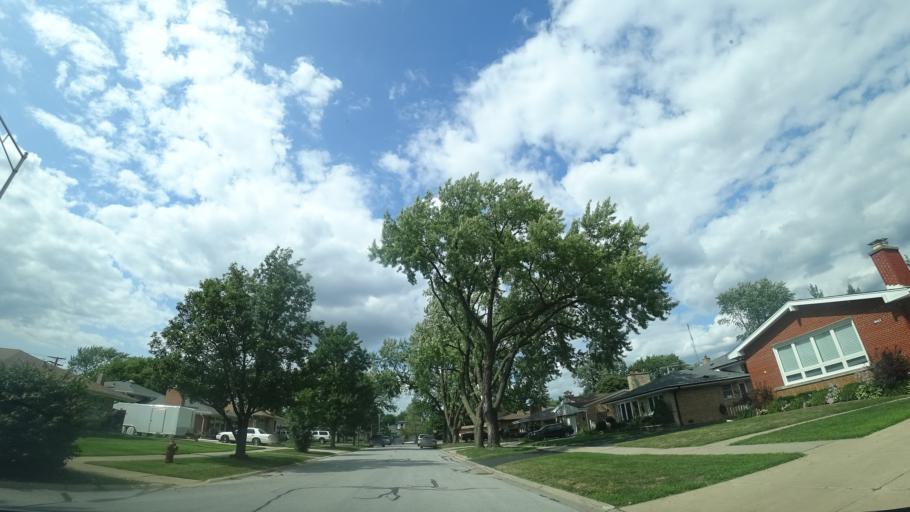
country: US
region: Illinois
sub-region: Cook County
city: Merrionette Park
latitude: 41.6958
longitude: -87.7260
